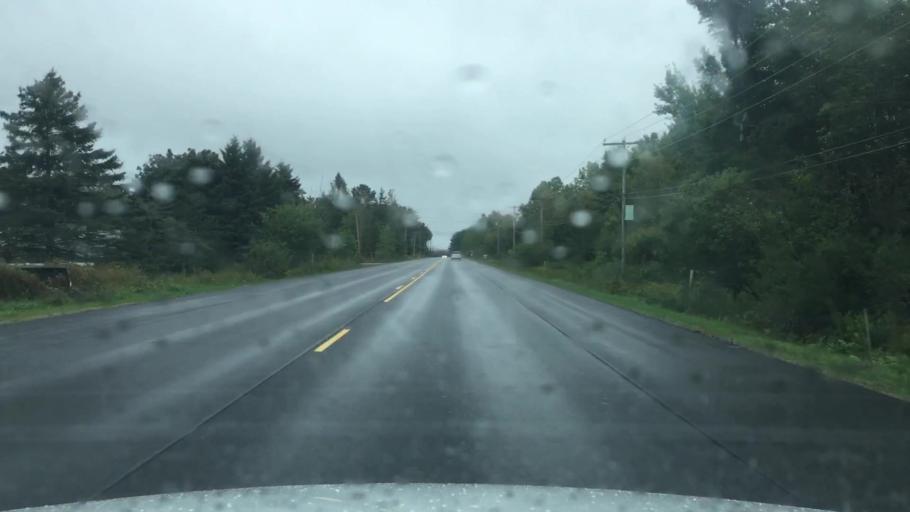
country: US
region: Maine
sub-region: Penobscot County
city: Hampden
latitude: 44.7595
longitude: -68.8462
